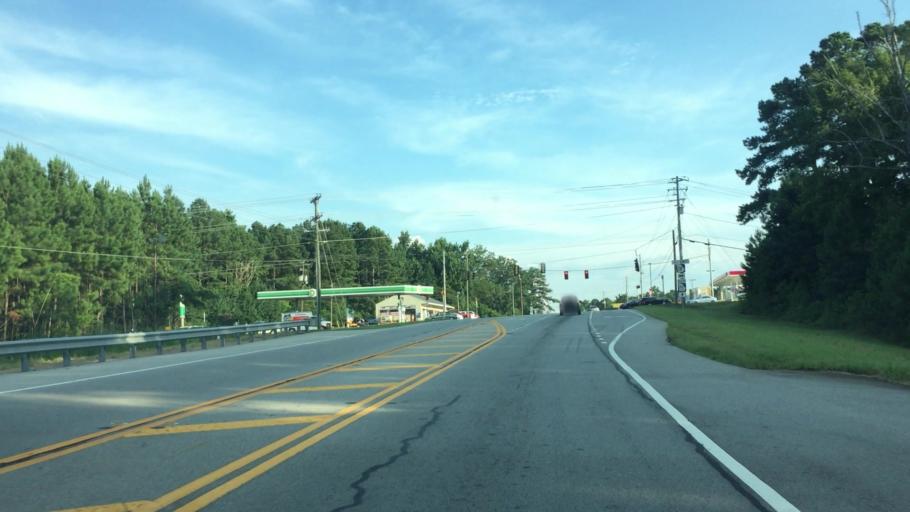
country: US
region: Georgia
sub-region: Henry County
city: Stockbridge
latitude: 33.5864
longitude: -84.1497
